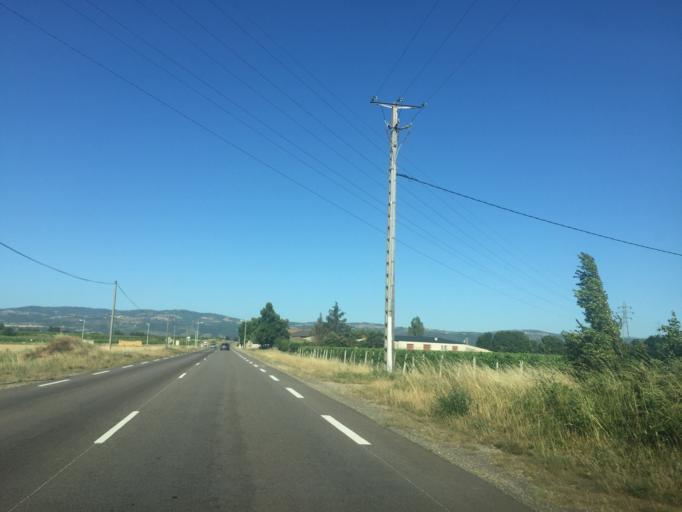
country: FR
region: Rhone-Alpes
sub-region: Departement de la Drome
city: Beaumont-Monteux
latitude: 45.0248
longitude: 4.9122
